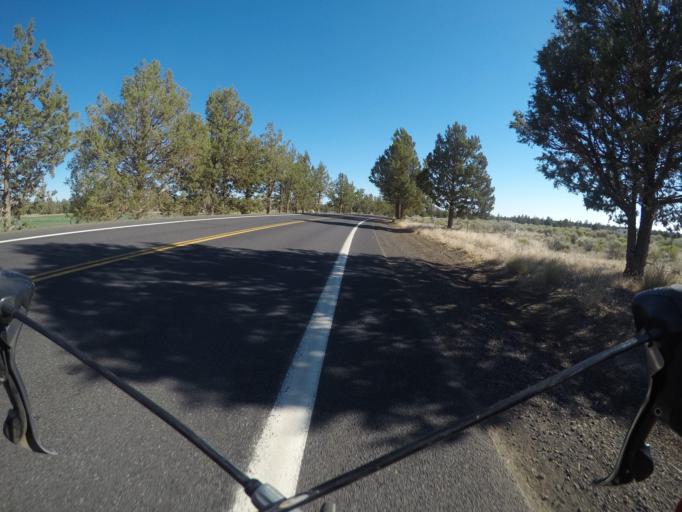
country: US
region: Oregon
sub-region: Deschutes County
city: Bend
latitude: 44.2088
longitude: -121.3188
